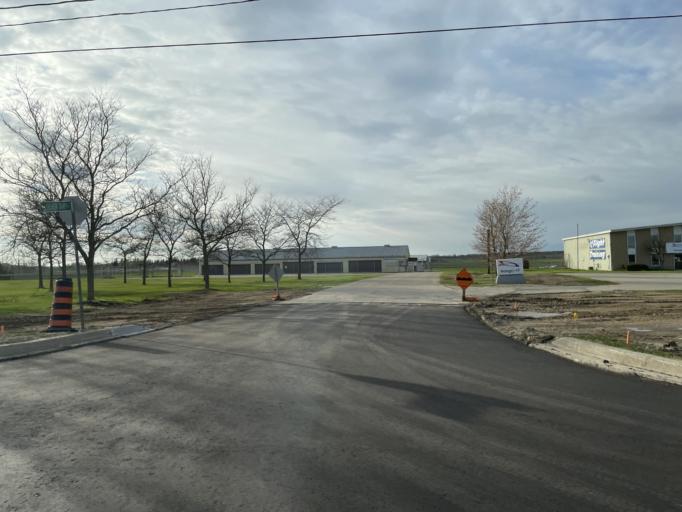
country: CA
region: Ontario
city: Cambridge
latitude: 43.4536
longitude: -80.3901
